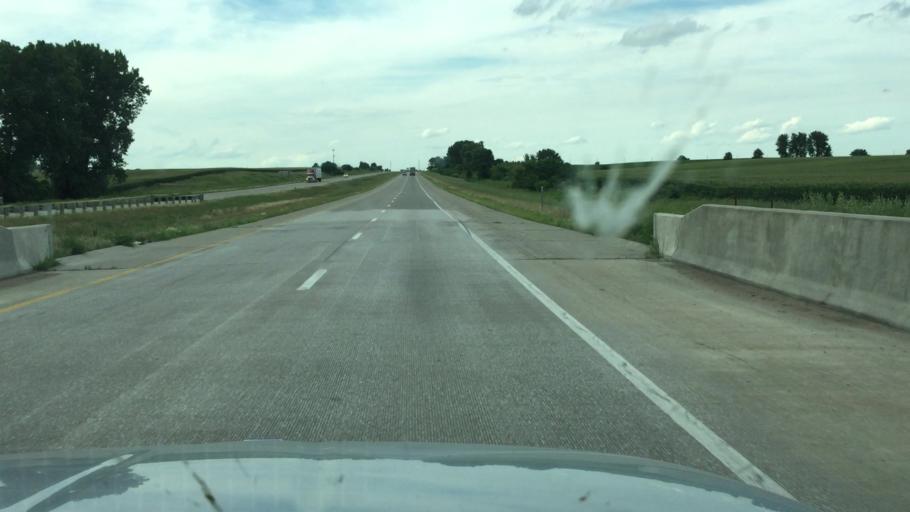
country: US
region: Iowa
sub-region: Scott County
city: Walcott
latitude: 41.5557
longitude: -90.6781
